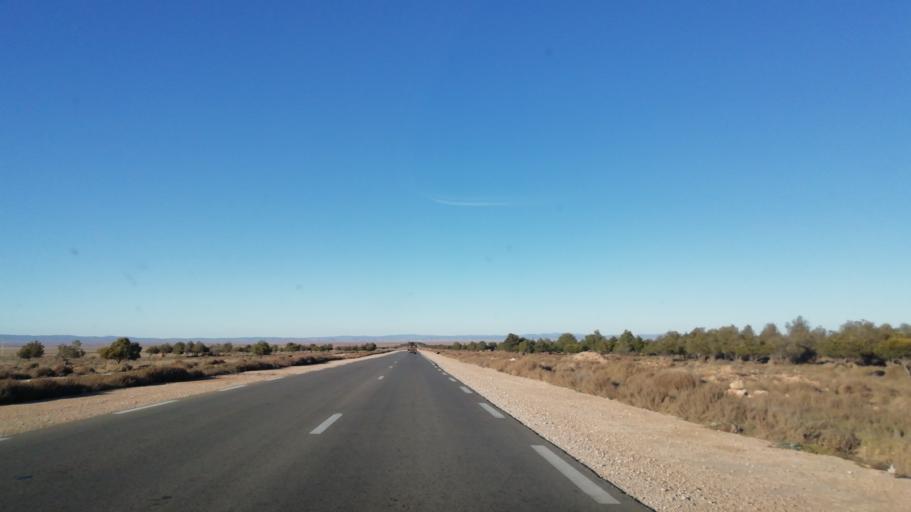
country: DZ
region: Tlemcen
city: Sebdou
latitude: 34.3200
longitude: -1.2631
